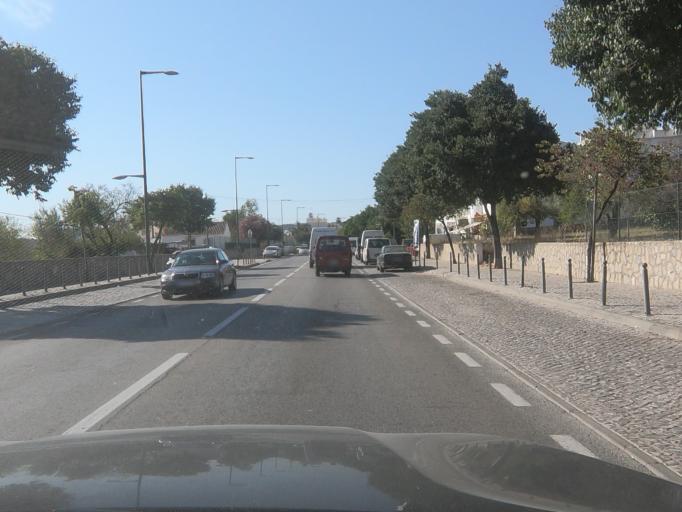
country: PT
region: Faro
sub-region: Loule
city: Loule
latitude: 37.1323
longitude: -8.0189
